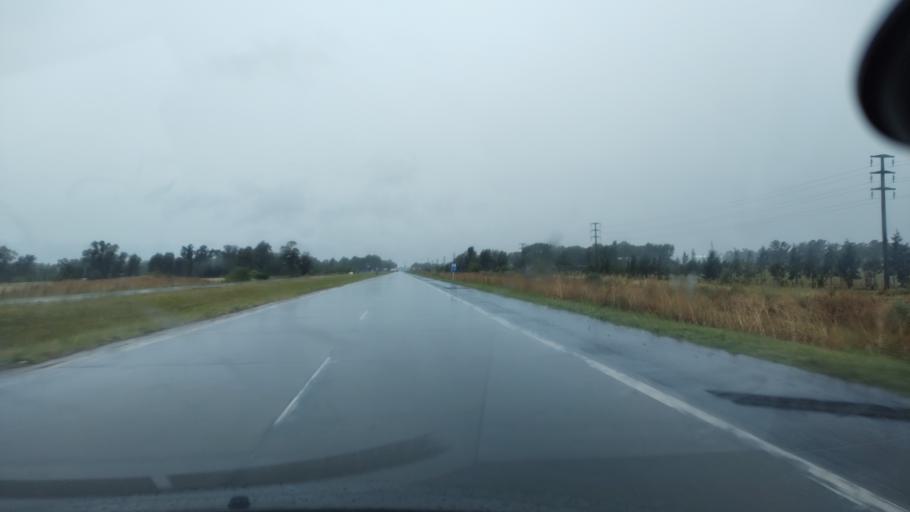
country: AR
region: Buenos Aires
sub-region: Partido de San Vicente
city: San Vicente
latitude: -35.0588
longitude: -58.4515
